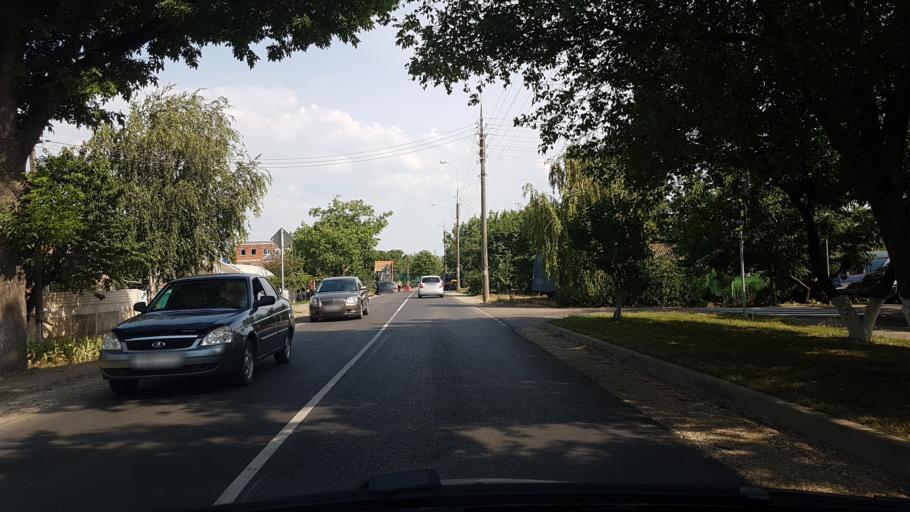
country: RU
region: Krasnodarskiy
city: Pashkovskiy
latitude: 45.0274
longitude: 39.1255
